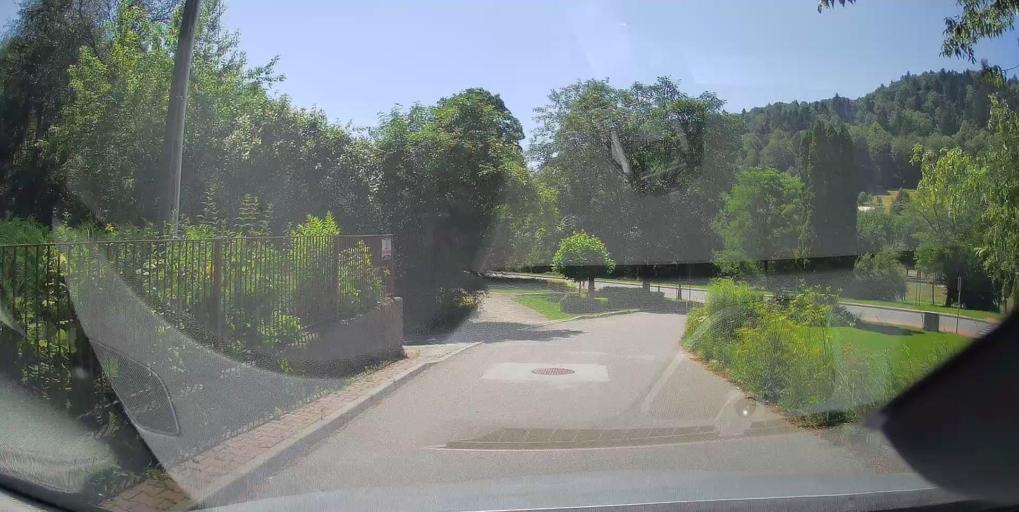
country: PL
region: Lesser Poland Voivodeship
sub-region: Powiat nowosadecki
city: Muszyna
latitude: 49.3558
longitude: 20.8890
